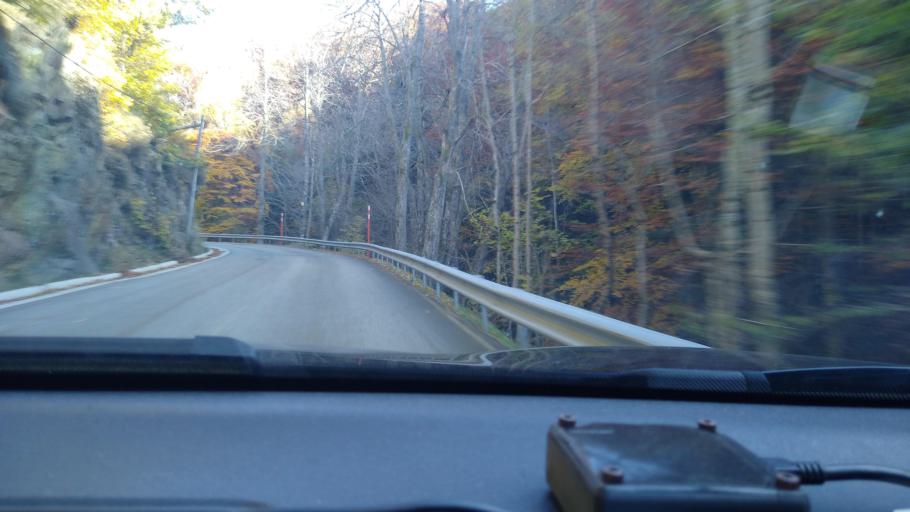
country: FR
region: Midi-Pyrenees
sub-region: Departement de l'Ariege
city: Ax-les-Thermes
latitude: 42.7188
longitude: 1.9083
